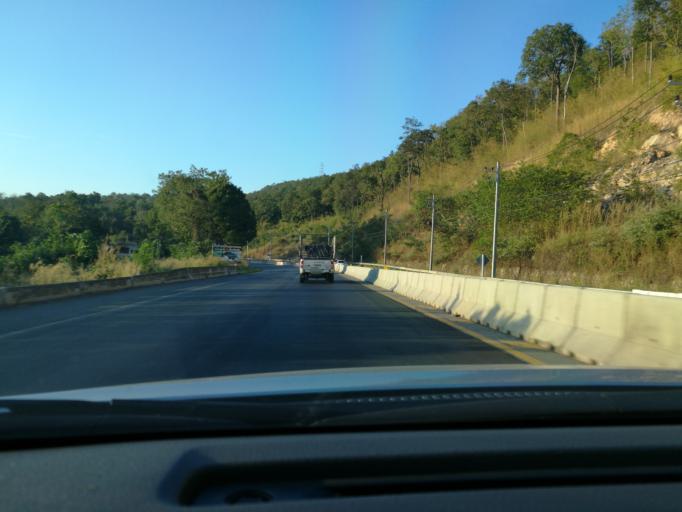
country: TH
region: Phitsanulok
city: Wang Thong
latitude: 16.8521
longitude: 100.5155
